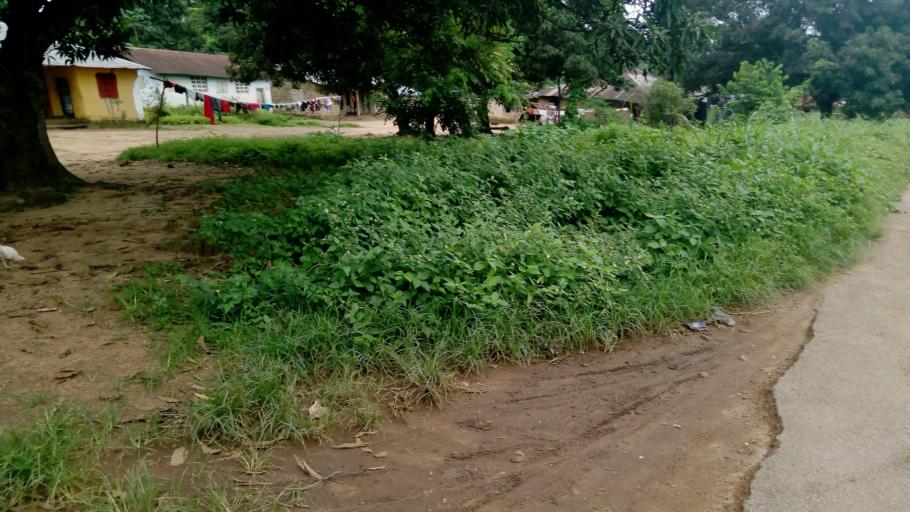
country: SL
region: Northern Province
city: Port Loko
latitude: 8.5068
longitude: -12.7611
